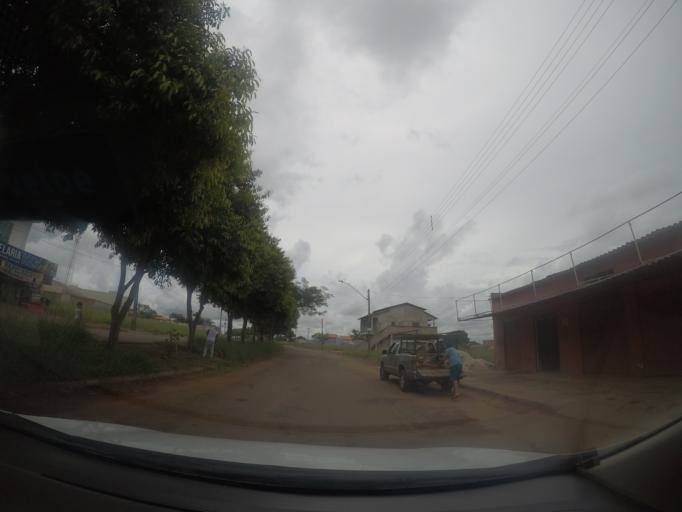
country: BR
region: Goias
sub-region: Trindade
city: Trindade
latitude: -16.6911
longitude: -49.3888
